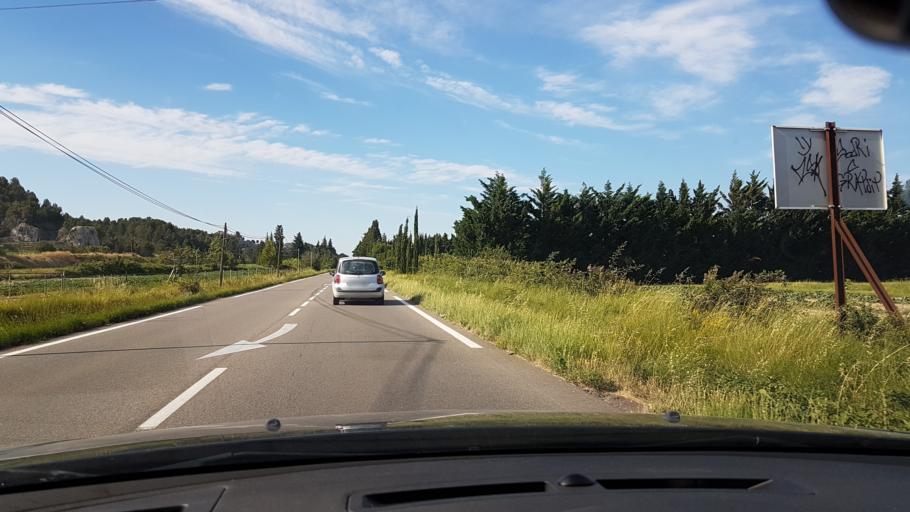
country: FR
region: Provence-Alpes-Cote d'Azur
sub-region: Departement des Bouches-du-Rhone
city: Graveson
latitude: 43.8658
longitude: 4.7699
